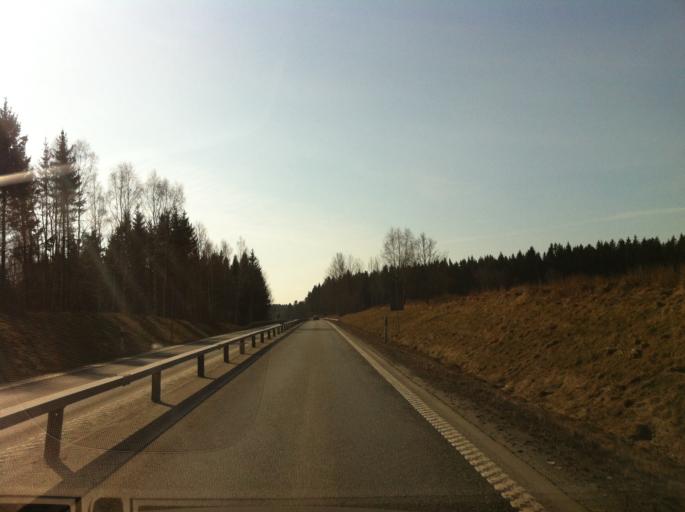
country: SE
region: Joenkoeping
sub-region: Jonkopings Kommun
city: Bankeryd
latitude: 57.8398
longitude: 14.1059
